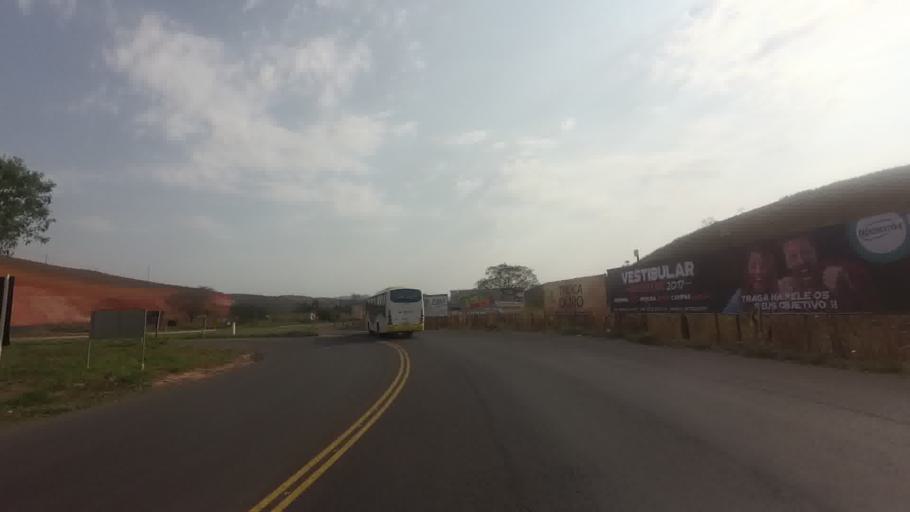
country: BR
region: Rio de Janeiro
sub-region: Itaperuna
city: Itaperuna
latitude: -21.2583
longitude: -41.7696
